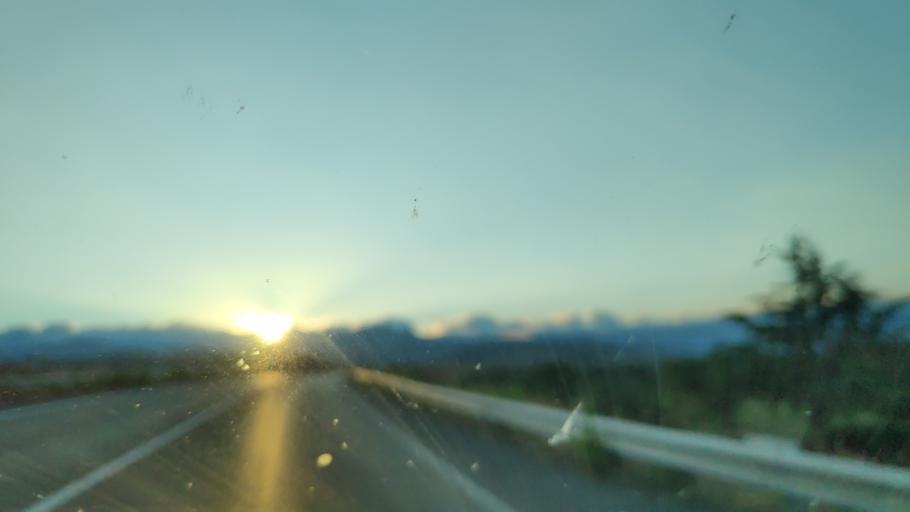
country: IT
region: Calabria
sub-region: Provincia di Reggio Calabria
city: Marina di Gioiosa Ionica
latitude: 38.2936
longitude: 16.3161
